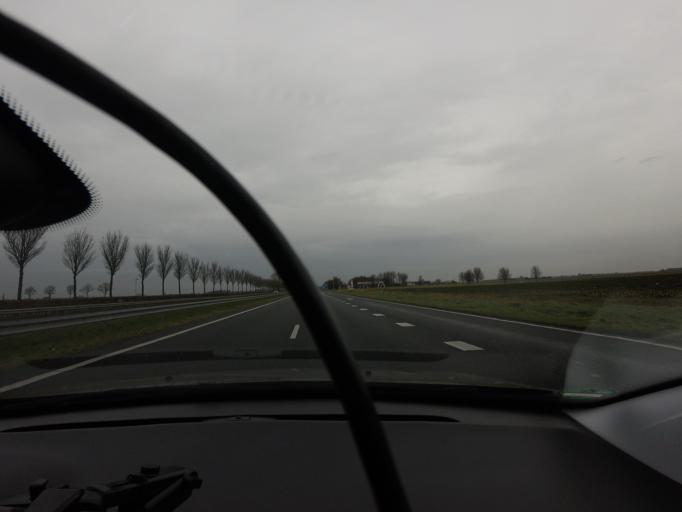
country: NL
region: North Holland
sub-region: Gemeente Medemblik
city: Opperdoes
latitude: 52.7094
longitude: 5.0281
